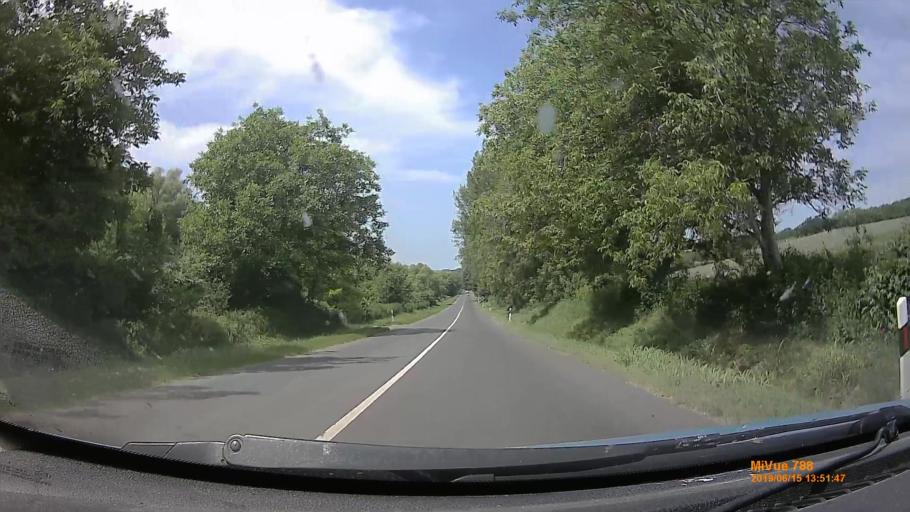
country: HU
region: Tolna
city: Iregszemcse
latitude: 46.7583
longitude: 18.1609
